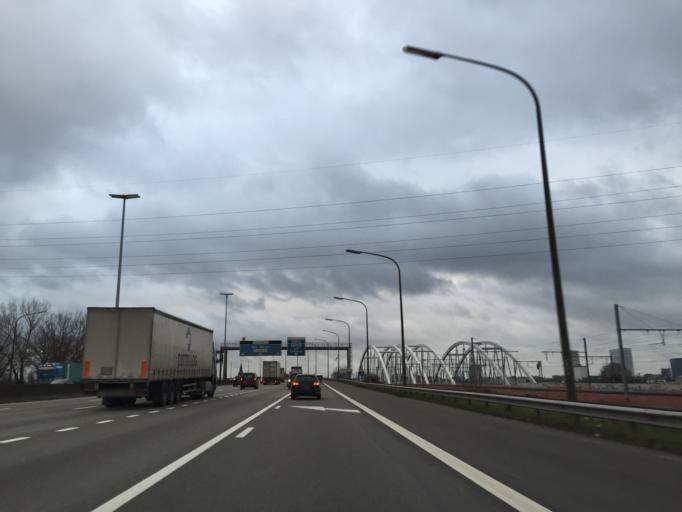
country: BE
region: Flanders
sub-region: Provincie Antwerpen
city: Antwerpen
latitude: 51.2414
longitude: 4.4260
